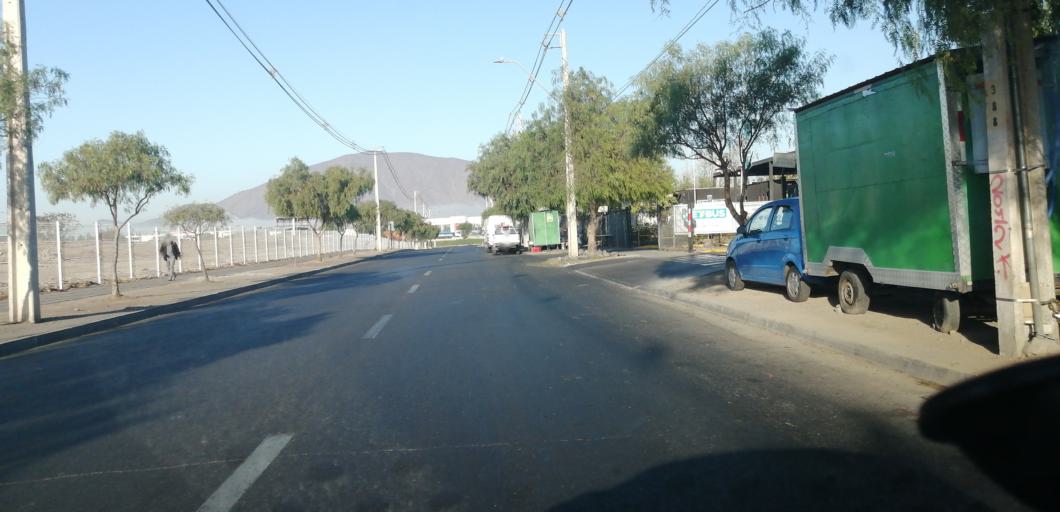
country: CL
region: Santiago Metropolitan
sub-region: Provincia de Santiago
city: Lo Prado
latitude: -33.4346
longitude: -70.7824
